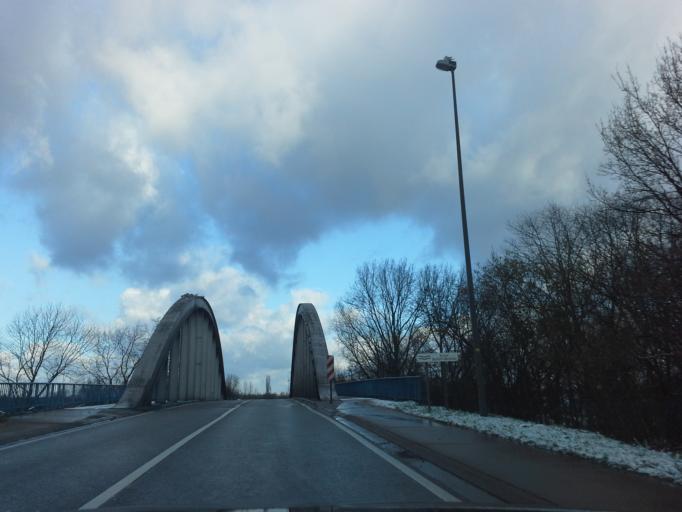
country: BE
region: Flanders
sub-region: Provincie Limburg
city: Neerpelt
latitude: 51.2321
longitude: 5.4448
